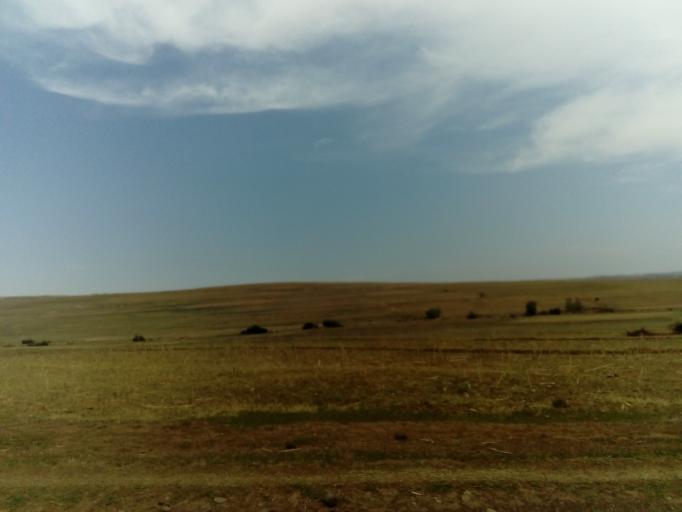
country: LS
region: Berea
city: Teyateyaneng
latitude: -29.1796
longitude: 27.7719
